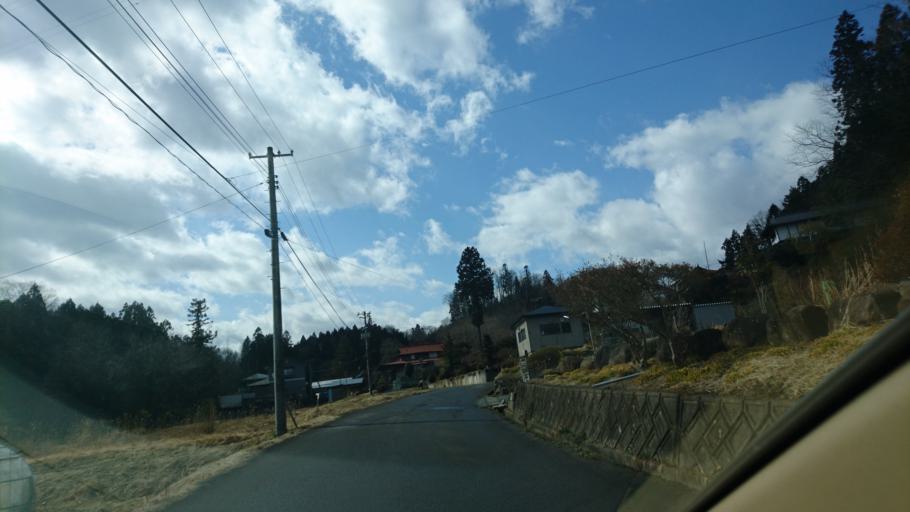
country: JP
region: Iwate
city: Ichinoseki
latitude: 38.9585
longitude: 141.1168
